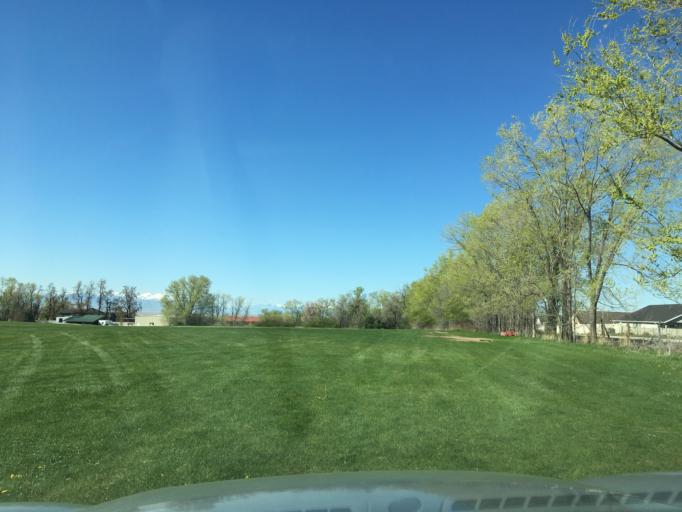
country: US
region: Utah
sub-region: Davis County
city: Layton
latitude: 41.0878
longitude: -111.9460
